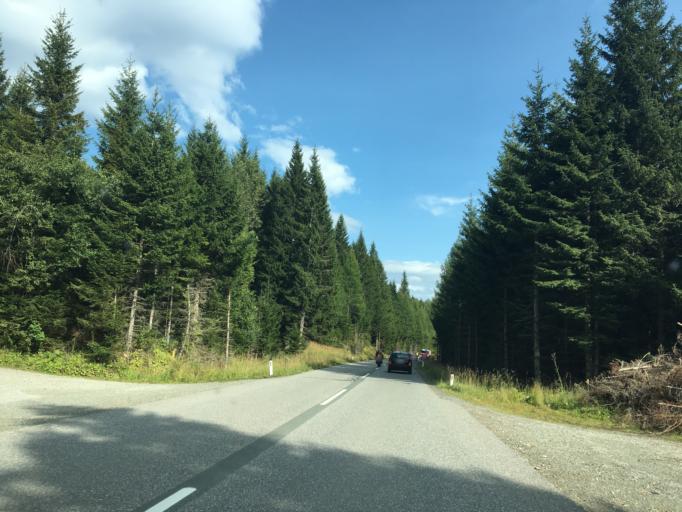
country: AT
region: Styria
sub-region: Politischer Bezirk Deutschlandsberg
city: Kloster
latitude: 46.8305
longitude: 15.0388
